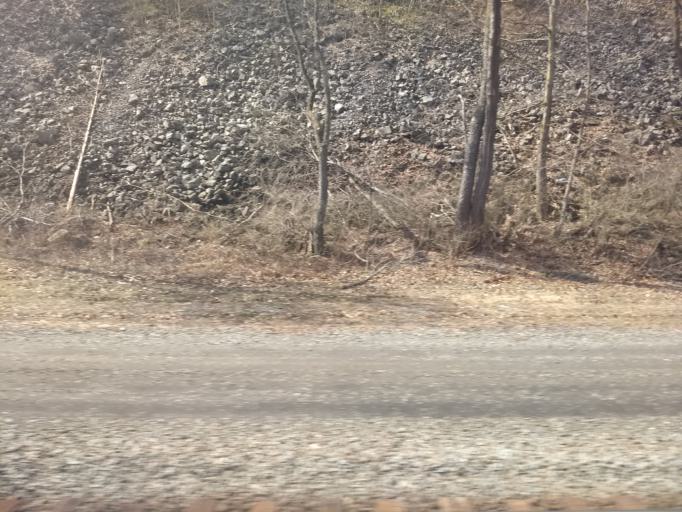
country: US
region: Pennsylvania
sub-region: Blair County
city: Tyrone
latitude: 40.6276
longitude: -78.1736
